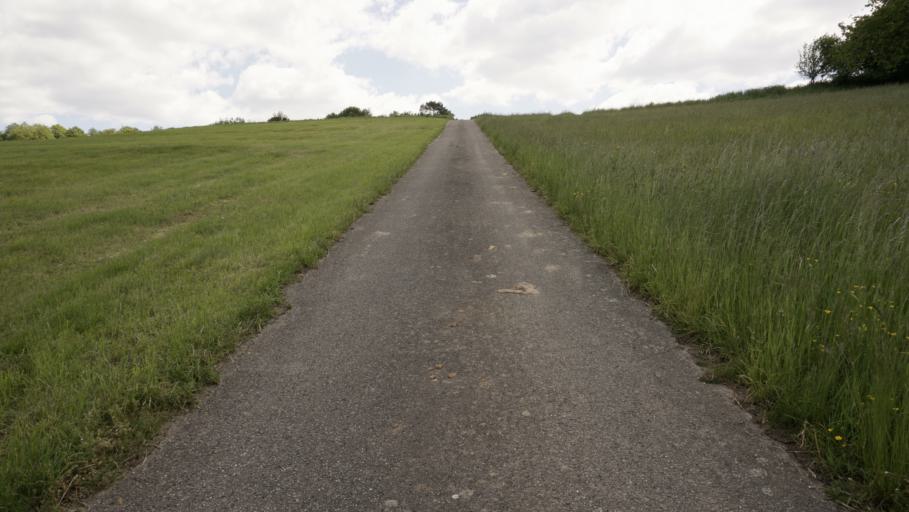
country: DE
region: Baden-Wuerttemberg
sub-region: Karlsruhe Region
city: Billigheim
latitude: 49.3865
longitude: 9.2164
